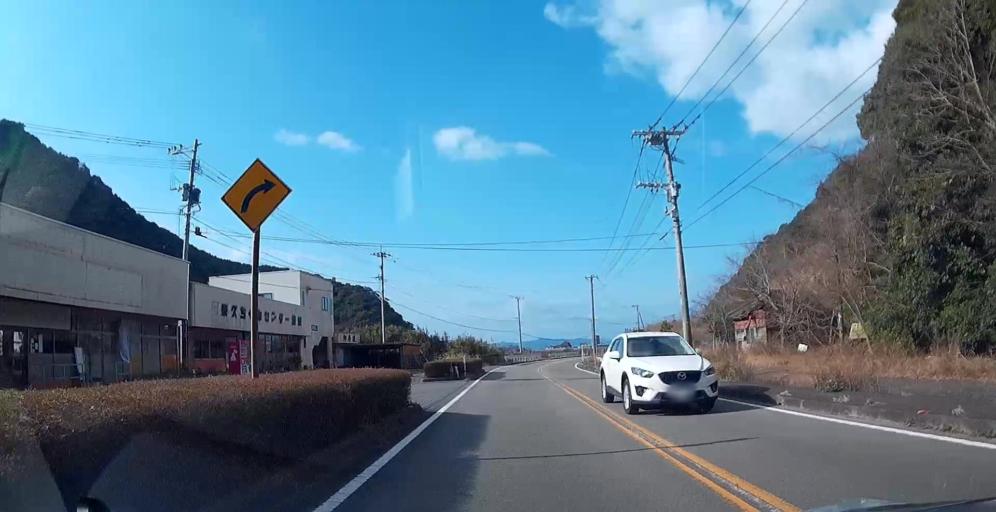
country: JP
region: Kumamoto
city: Yatsushiro
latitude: 32.4135
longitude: 130.5520
